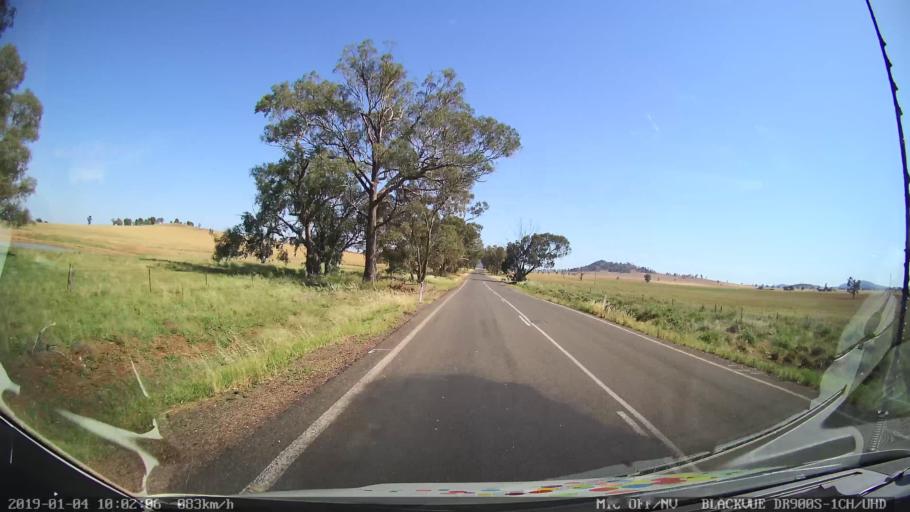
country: AU
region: New South Wales
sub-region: Cabonne
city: Canowindra
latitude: -33.4804
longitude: 148.3661
